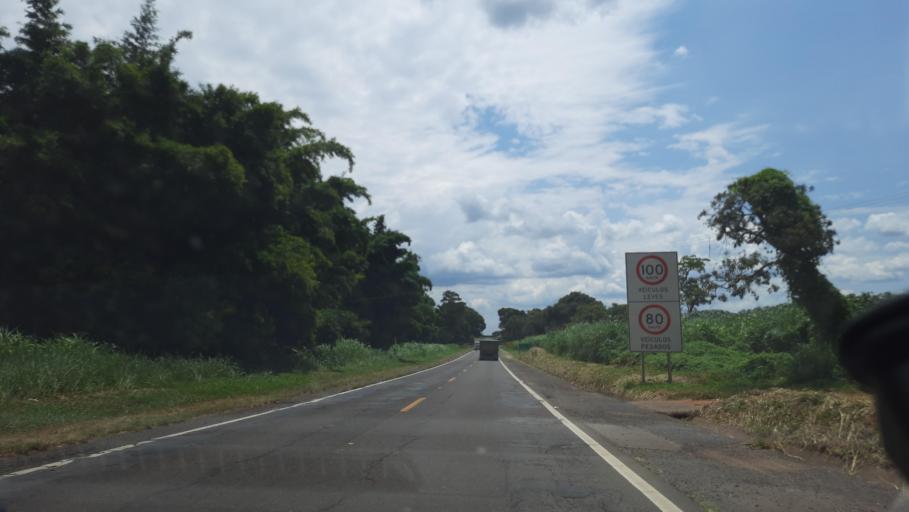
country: BR
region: Sao Paulo
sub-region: Mococa
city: Mococa
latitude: -21.5147
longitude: -47.0360
